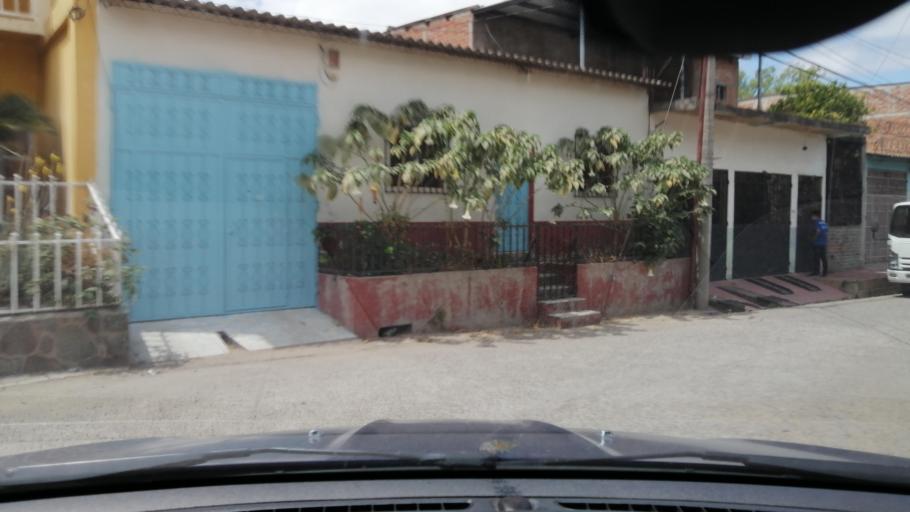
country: SV
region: Santa Ana
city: Metapan
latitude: 14.3350
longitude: -89.4431
